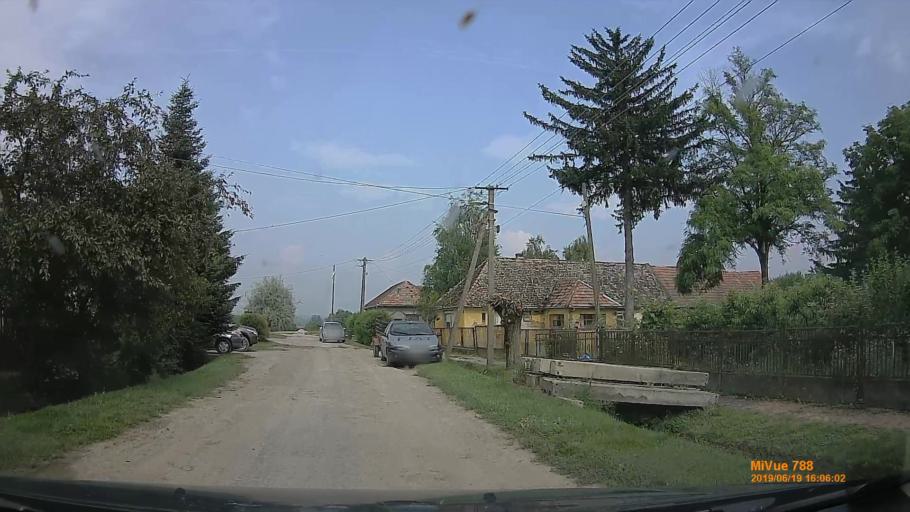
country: HU
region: Baranya
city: Szigetvar
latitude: 46.0738
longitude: 17.7865
